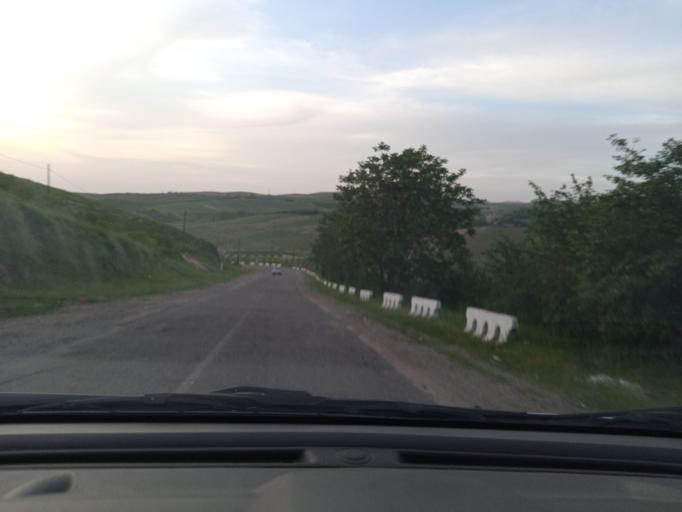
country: UZ
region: Toshkent
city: Parkent
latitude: 41.2397
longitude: 69.7331
